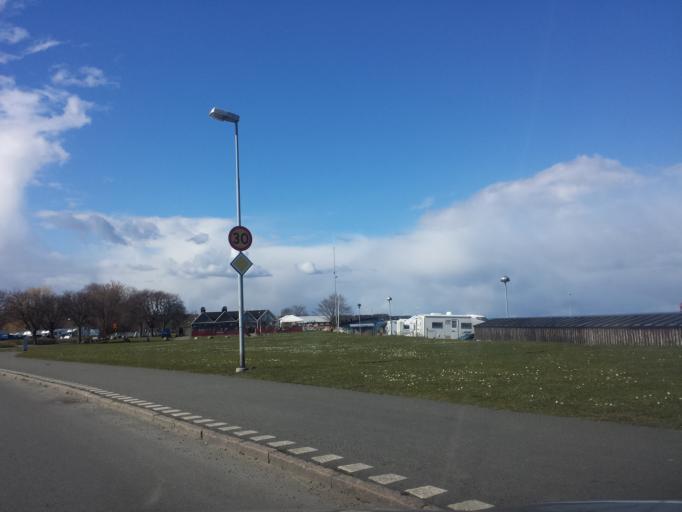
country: SE
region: Skane
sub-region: Simrishamns Kommun
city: Simrishamn
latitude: 55.5598
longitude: 14.3504
